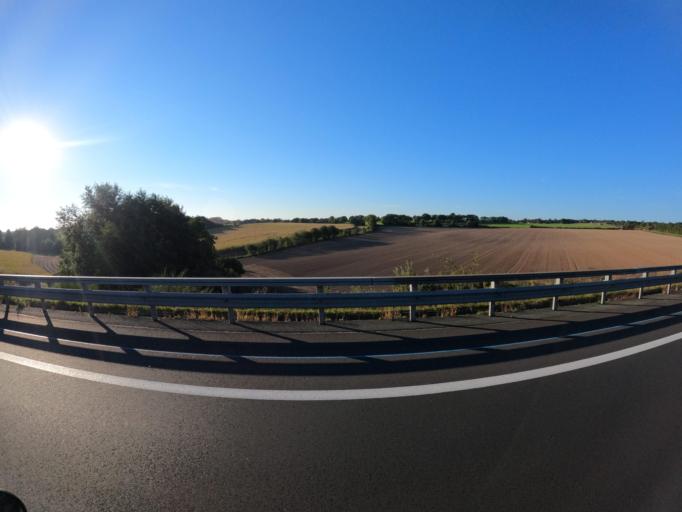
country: FR
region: Pays de la Loire
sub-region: Departement de la Vendee
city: La Gaubretiere
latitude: 46.9103
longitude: -1.0463
